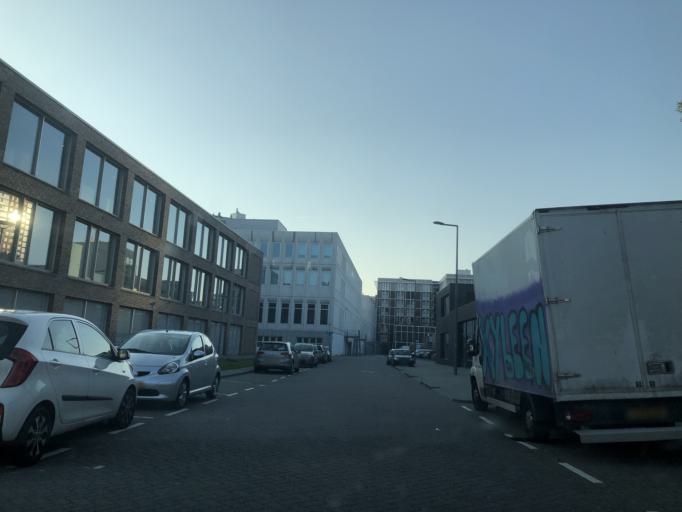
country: NL
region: South Holland
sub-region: Gemeente Rotterdam
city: Rotterdam
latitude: 51.8856
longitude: 4.4966
